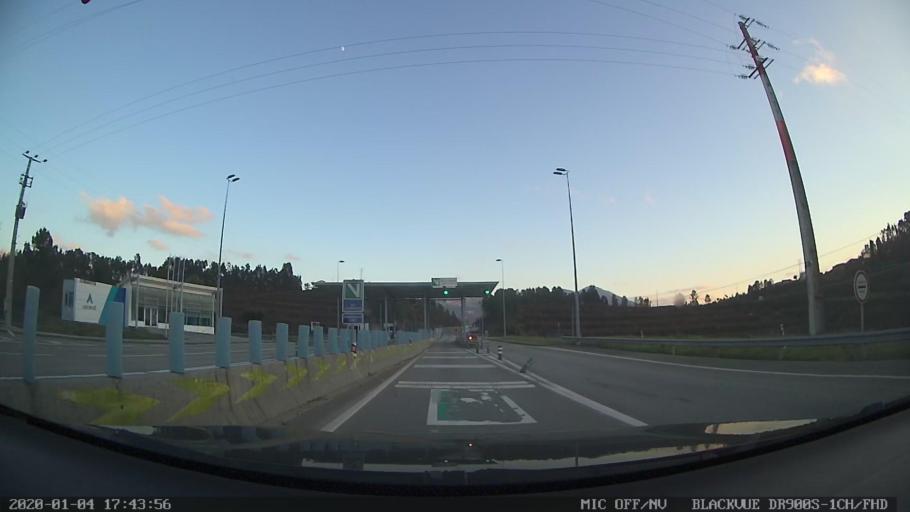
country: PT
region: Braga
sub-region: Cabeceiras de Basto
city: Cabeceiras de Basto
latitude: 41.4766
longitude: -7.9494
